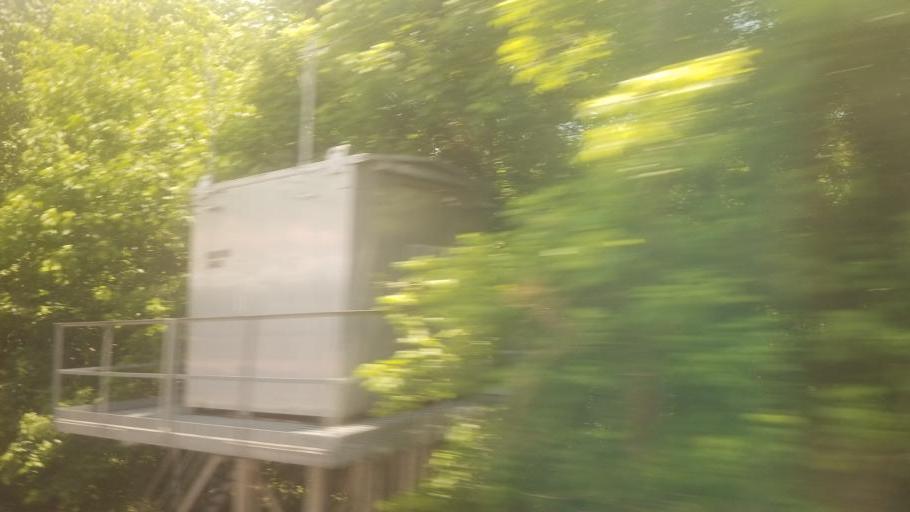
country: US
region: West Virginia
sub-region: Jefferson County
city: Bolivar
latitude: 39.3256
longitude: -77.7119
